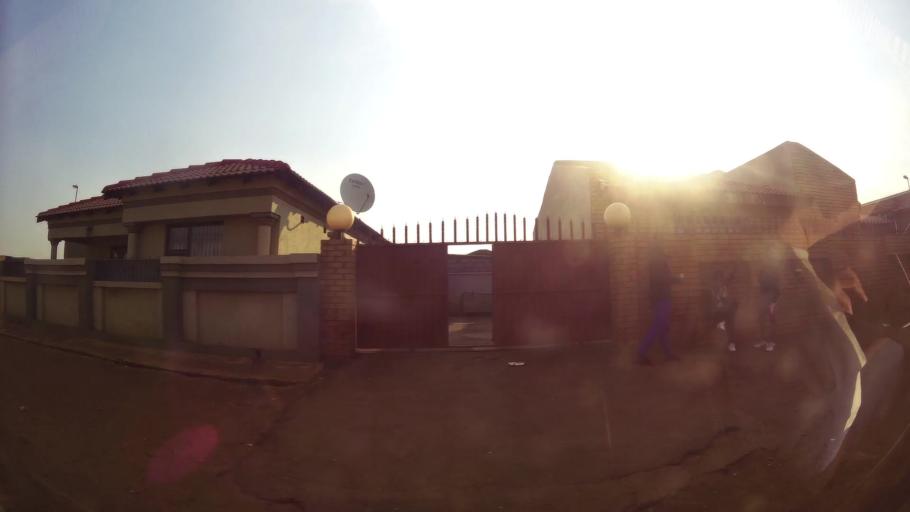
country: ZA
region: Gauteng
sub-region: Ekurhuleni Metropolitan Municipality
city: Germiston
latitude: -26.3695
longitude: 28.1976
